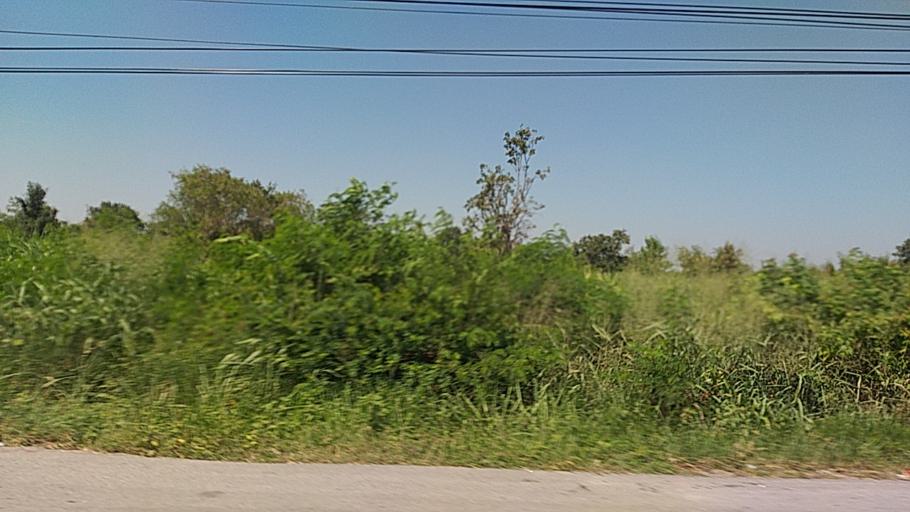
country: TH
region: Nakhon Ratchasima
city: Sung Noen
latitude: 14.8860
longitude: 101.8688
